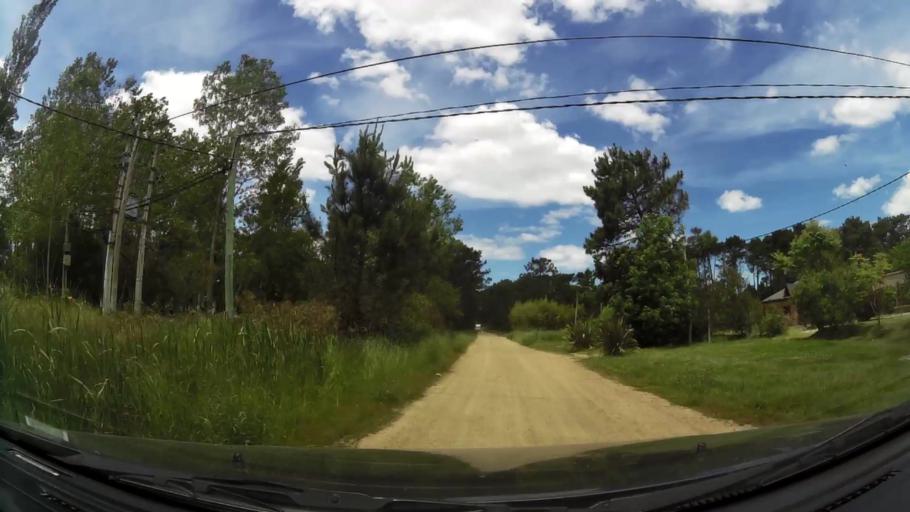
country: UY
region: Canelones
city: Empalme Olmos
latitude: -34.7938
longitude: -55.8947
